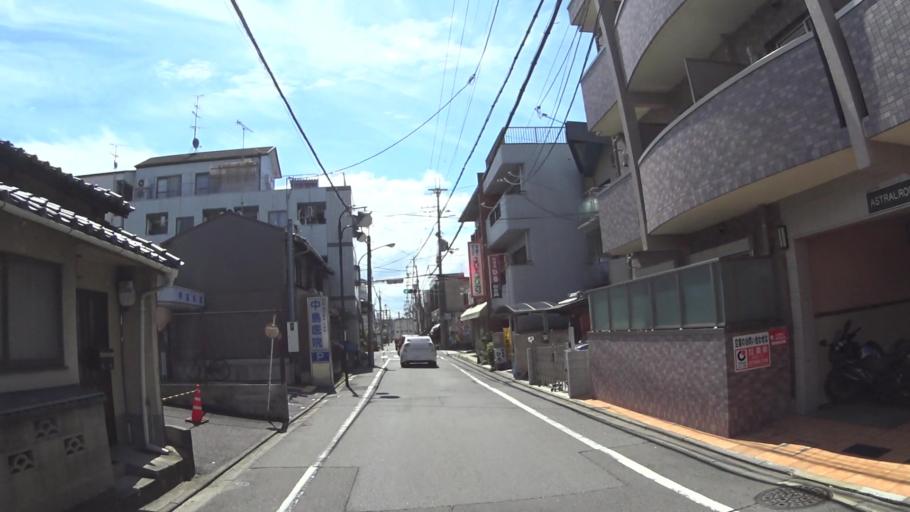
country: JP
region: Kyoto
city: Muko
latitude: 34.9487
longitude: 135.7666
